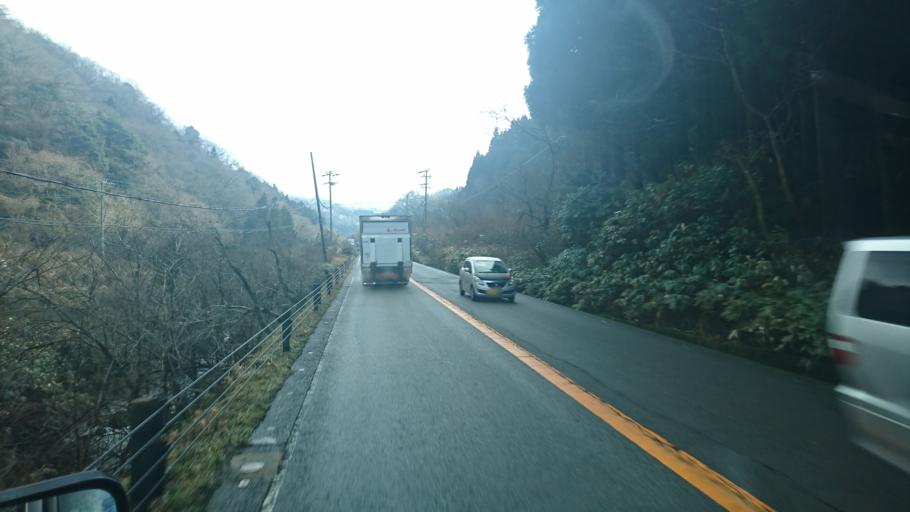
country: JP
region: Tottori
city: Tottori
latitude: 35.5313
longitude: 134.5162
